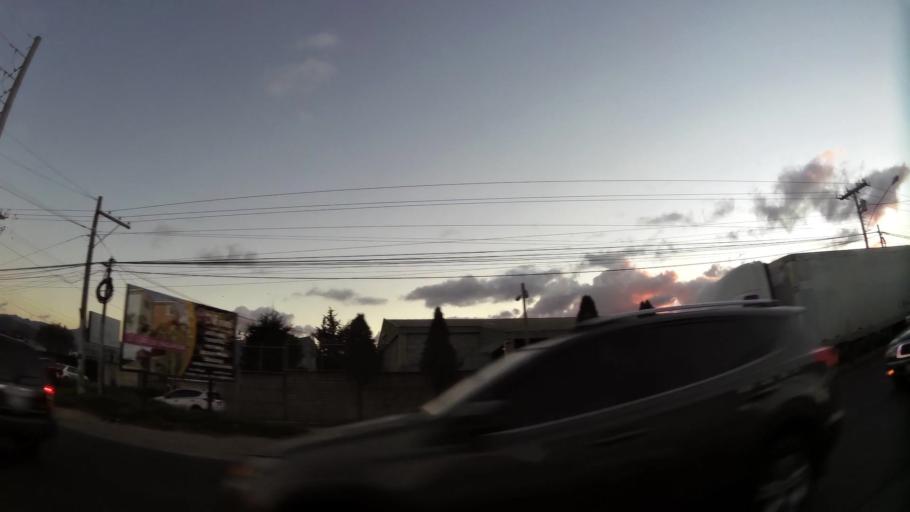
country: GT
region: Quetzaltenango
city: Olintepeque
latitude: 14.8617
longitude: -91.5271
